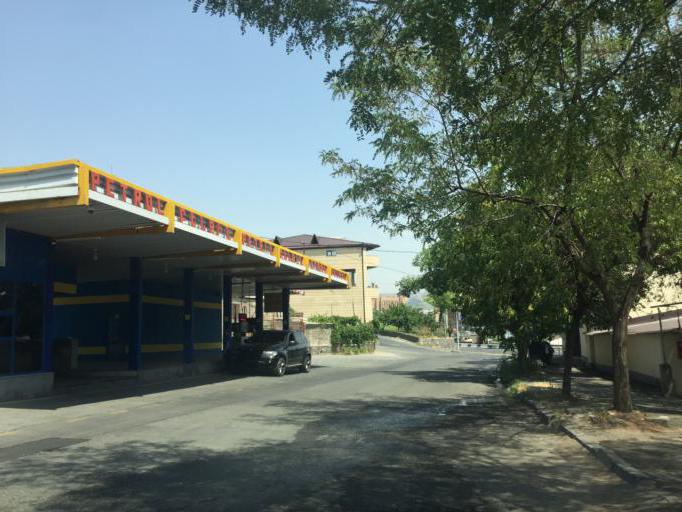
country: AM
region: Yerevan
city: Yerevan
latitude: 40.1742
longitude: 44.4942
